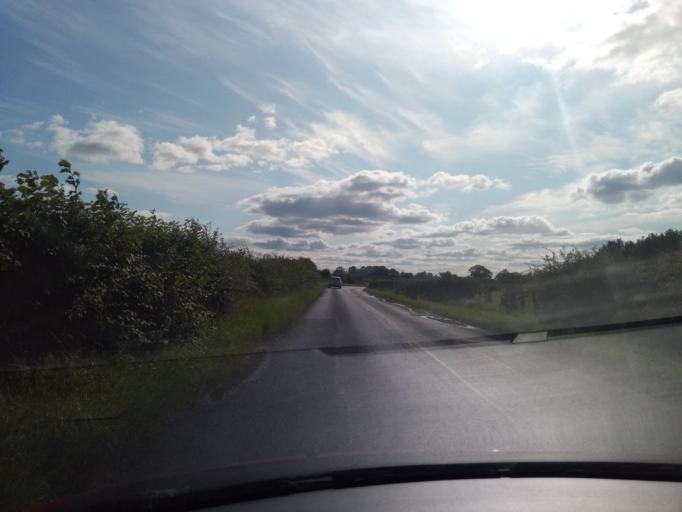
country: GB
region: Scotland
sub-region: The Scottish Borders
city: Allanton
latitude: 55.7466
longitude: -2.1622
